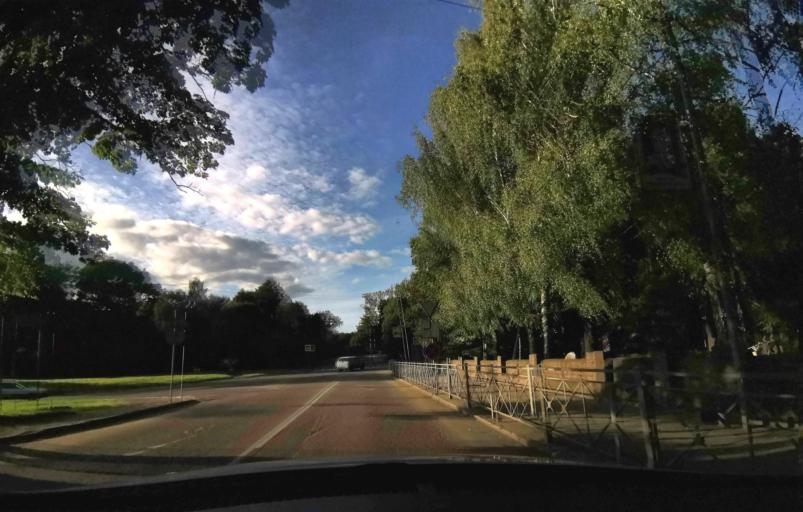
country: RU
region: Kaliningrad
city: Chernyakhovsk
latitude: 54.6280
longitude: 21.8125
